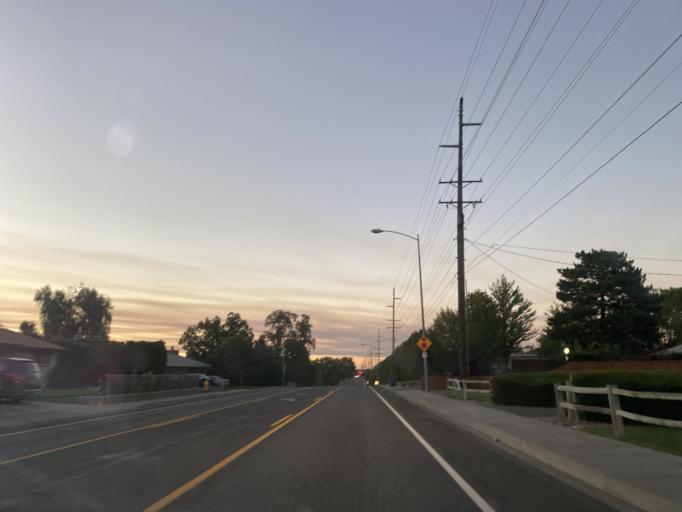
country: US
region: Washington
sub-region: Benton County
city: Kennewick
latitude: 46.2012
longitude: -119.1696
